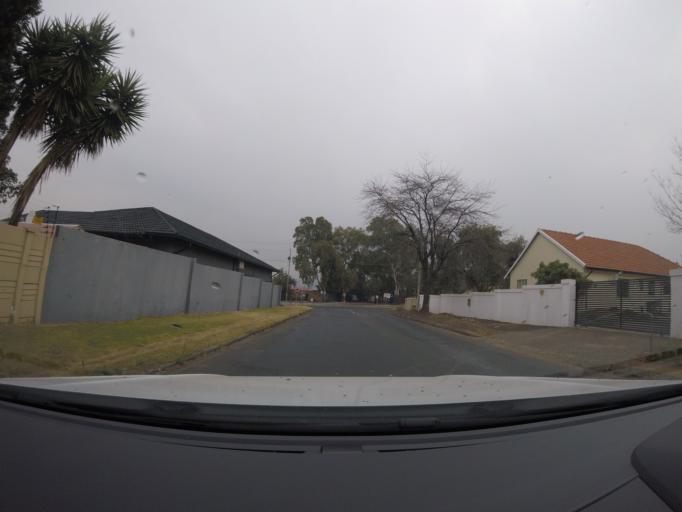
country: ZA
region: Gauteng
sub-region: City of Johannesburg Metropolitan Municipality
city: Modderfontein
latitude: -26.1477
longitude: 28.1501
